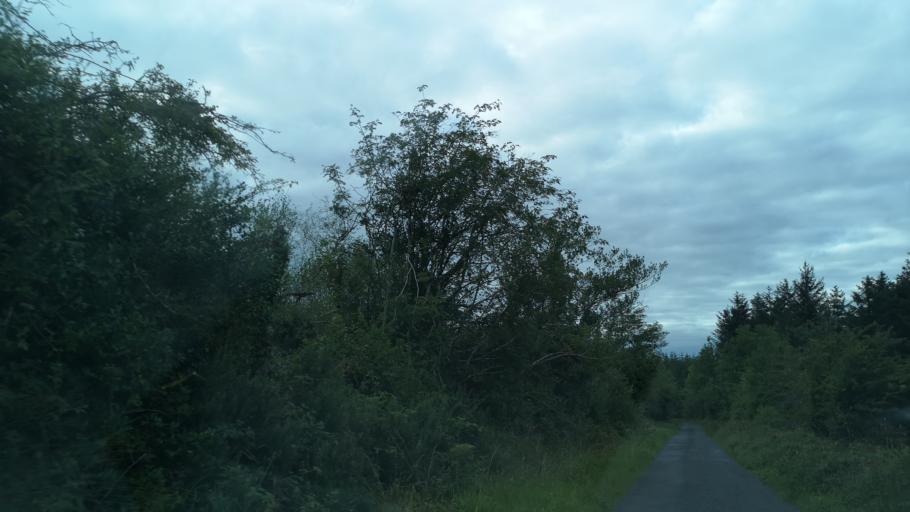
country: IE
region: Connaught
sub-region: County Galway
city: Loughrea
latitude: 53.1363
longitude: -8.5218
